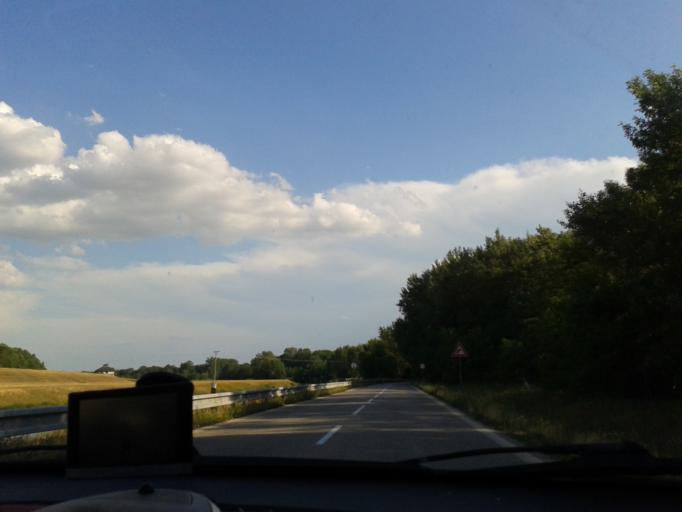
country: HU
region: Gyor-Moson-Sopron
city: Rajka
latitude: 48.0241
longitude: 17.2046
